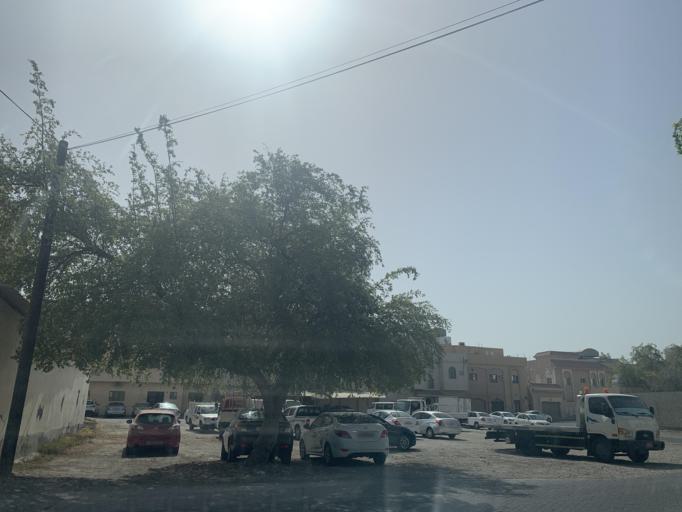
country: BH
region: Manama
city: Jidd Hafs
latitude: 26.2041
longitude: 50.5516
